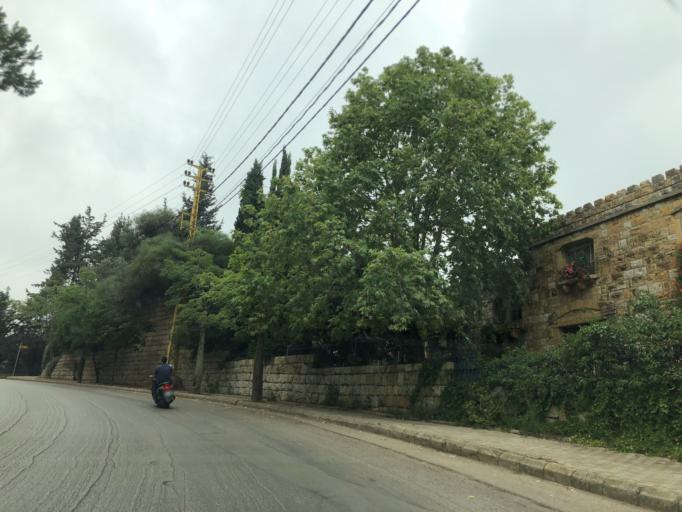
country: LB
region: Mont-Liban
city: Jdaidet el Matn
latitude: 33.8763
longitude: 35.6245
